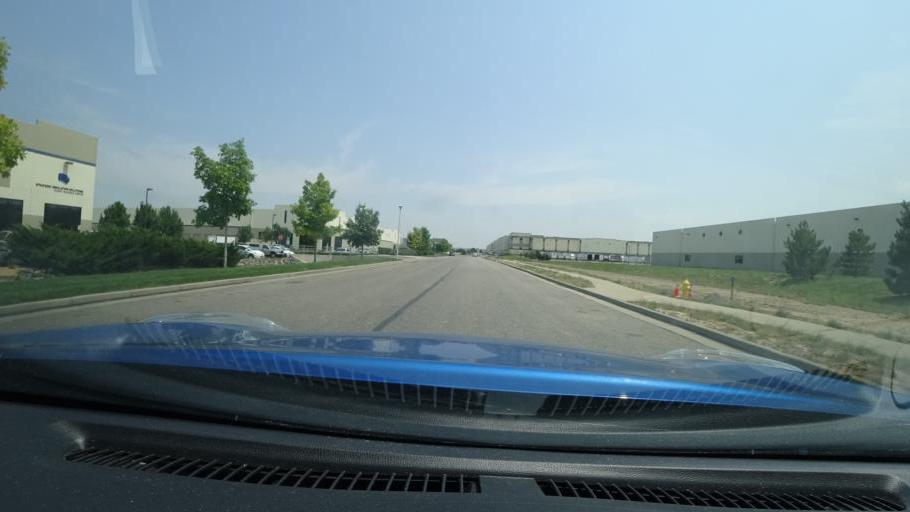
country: US
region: Colorado
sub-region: Adams County
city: Aurora
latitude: 39.7637
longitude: -104.7595
